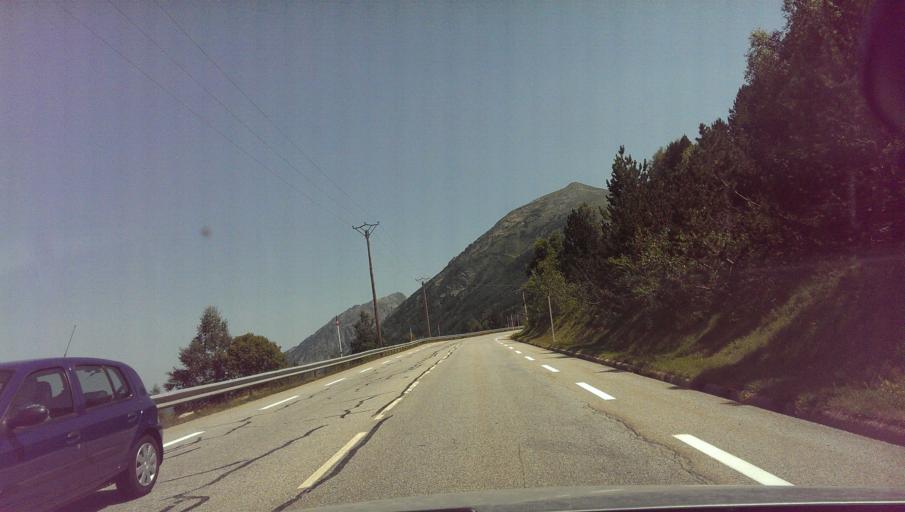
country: AD
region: Encamp
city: Pas de la Casa
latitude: 42.5665
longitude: 1.7841
